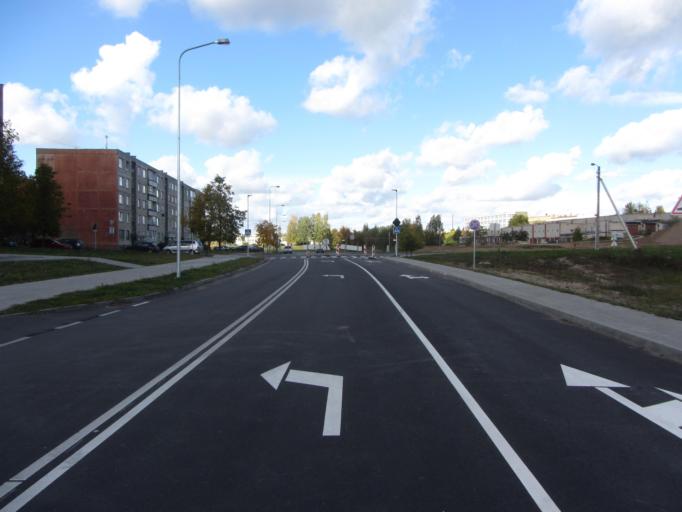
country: LT
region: Utenos apskritis
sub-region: Utena
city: Utena
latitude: 55.5065
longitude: 25.6161
